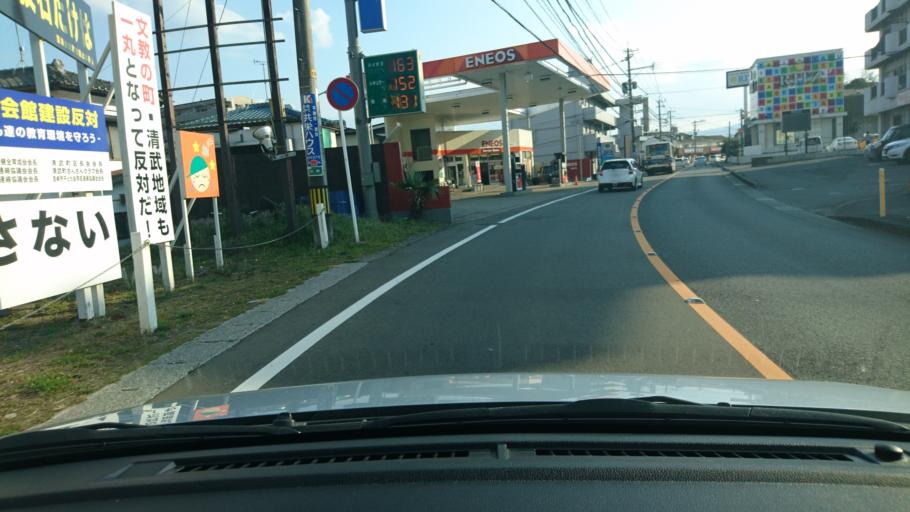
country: JP
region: Miyazaki
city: Miyazaki-shi
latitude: 31.8827
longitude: 131.4083
